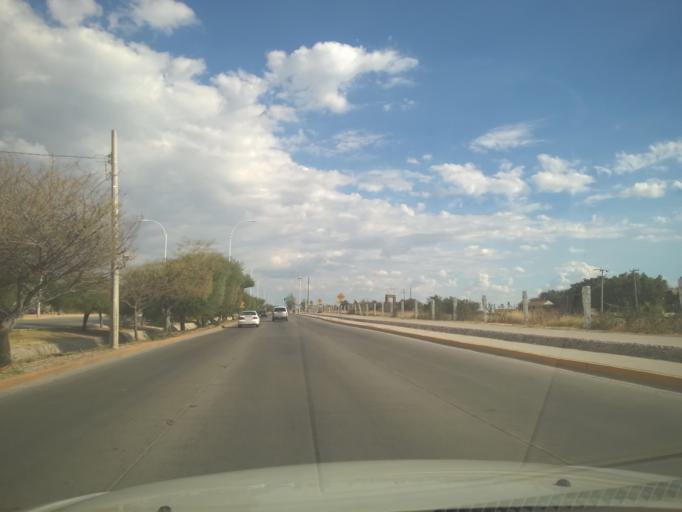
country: MX
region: Guanajuato
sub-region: Leon
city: San Jose de Duran (Los Troncoso)
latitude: 21.0709
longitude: -101.6429
